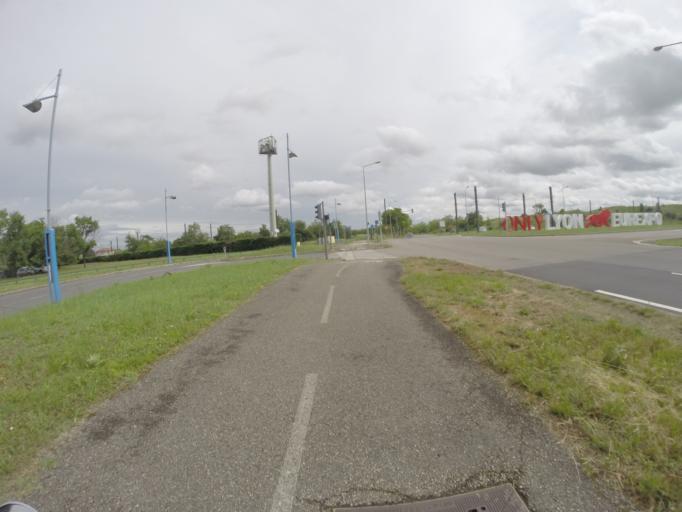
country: FR
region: Rhone-Alpes
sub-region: Departement du Rhone
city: Bron
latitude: 45.7386
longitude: 4.9352
